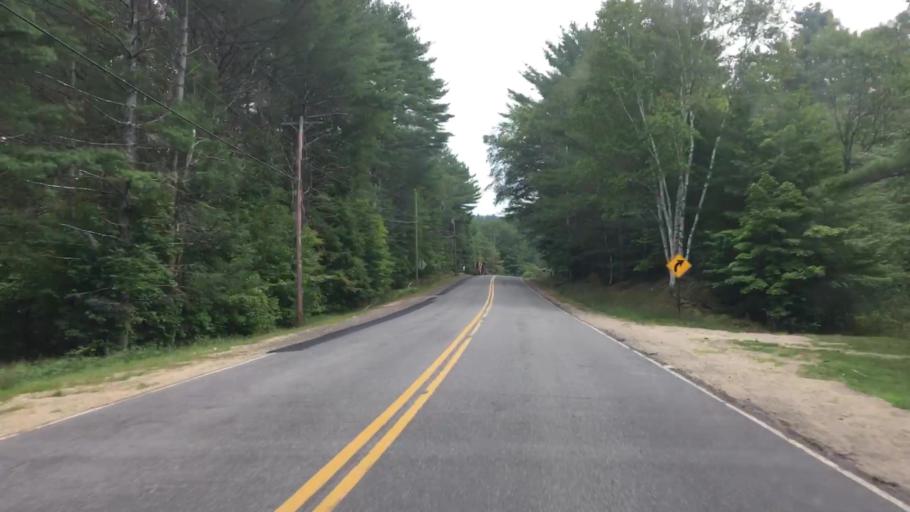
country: US
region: Maine
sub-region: Oxford County
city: Rumford
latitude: 44.5247
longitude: -70.6823
